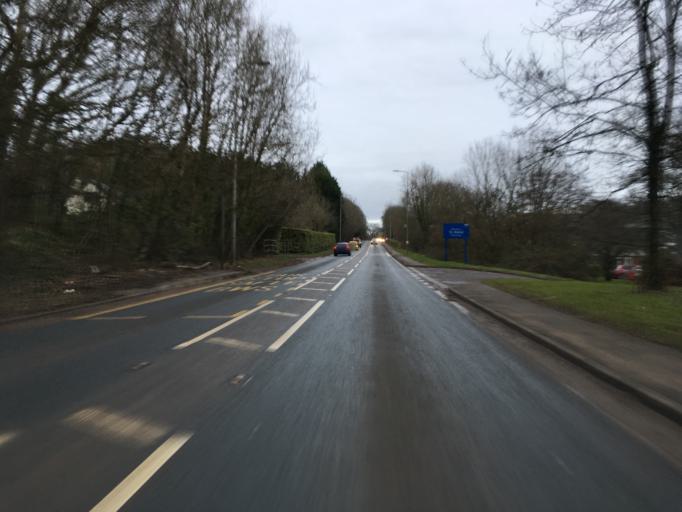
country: GB
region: Wales
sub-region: Cardiff
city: Pentyrch
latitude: 51.5114
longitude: -3.3012
